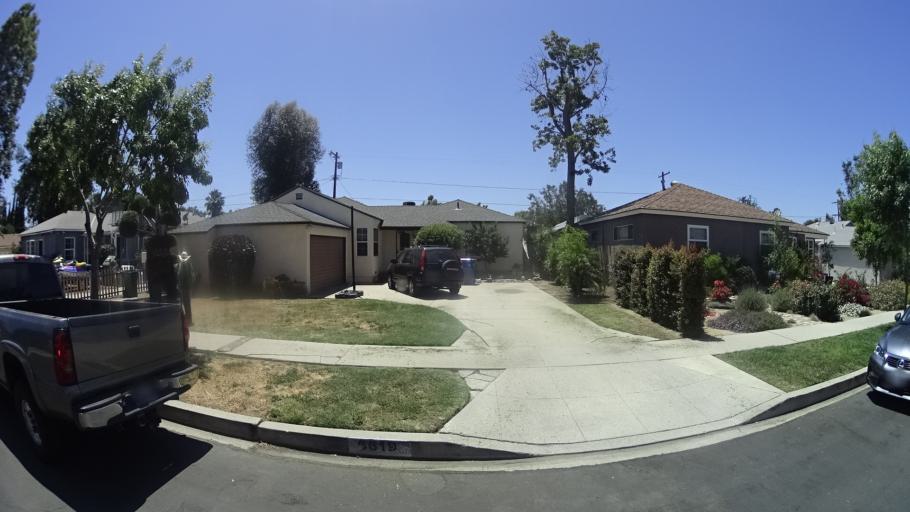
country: US
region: California
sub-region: Los Angeles County
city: Northridge
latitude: 34.1910
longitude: -118.5216
